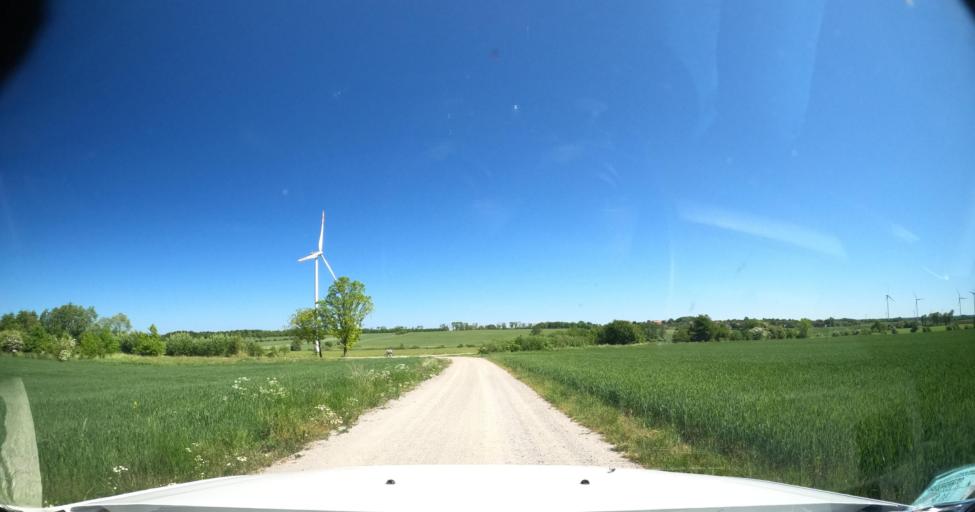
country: PL
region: Pomeranian Voivodeship
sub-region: Powiat slupski
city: Ustka
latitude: 54.5128
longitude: 16.7482
